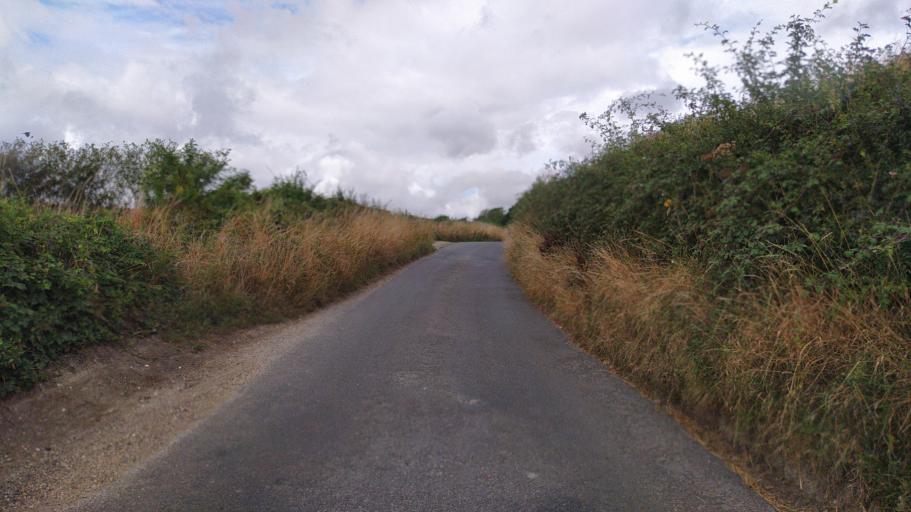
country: GB
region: England
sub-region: Hampshire
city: Petersfield
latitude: 50.9866
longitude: -0.9681
